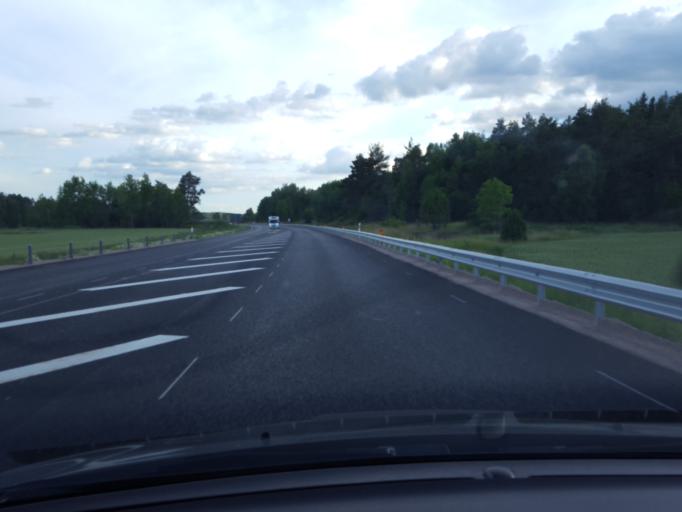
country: SE
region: Uppsala
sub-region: Osthammars Kommun
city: Gimo
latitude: 60.0703
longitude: 18.0925
